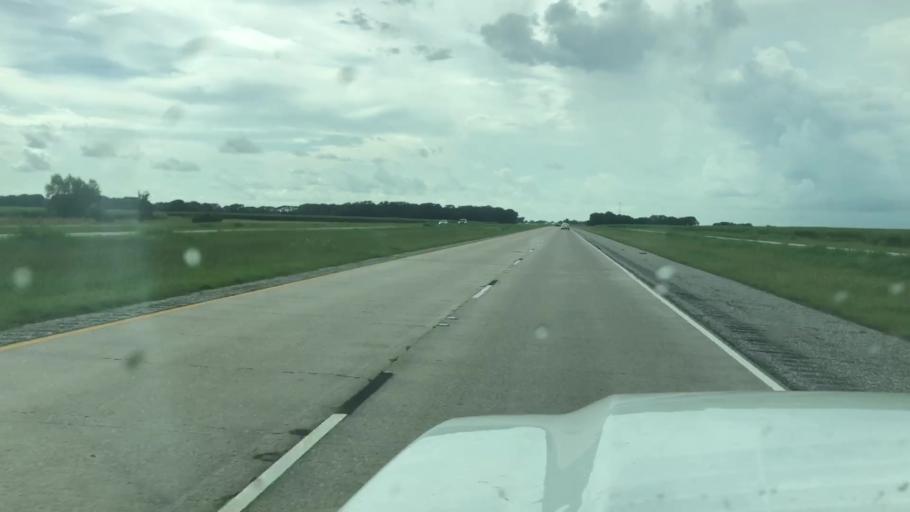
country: US
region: Louisiana
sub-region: Saint Mary Parish
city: Baldwin
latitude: 29.8523
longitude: -91.6008
